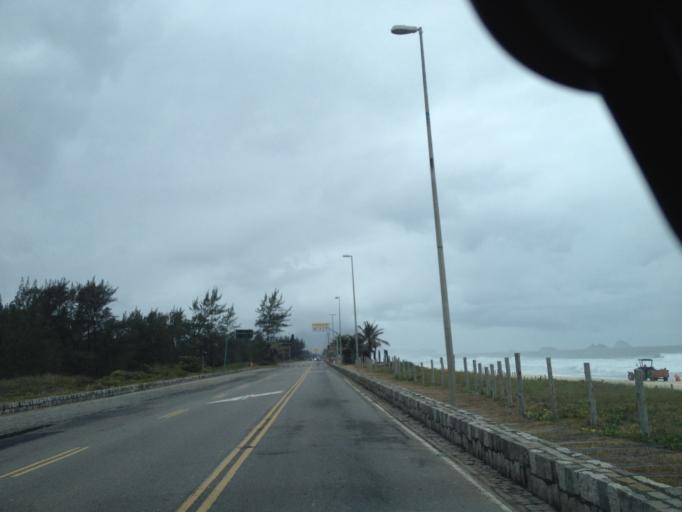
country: BR
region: Rio de Janeiro
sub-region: Nilopolis
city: Nilopolis
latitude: -23.0146
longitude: -43.4048
